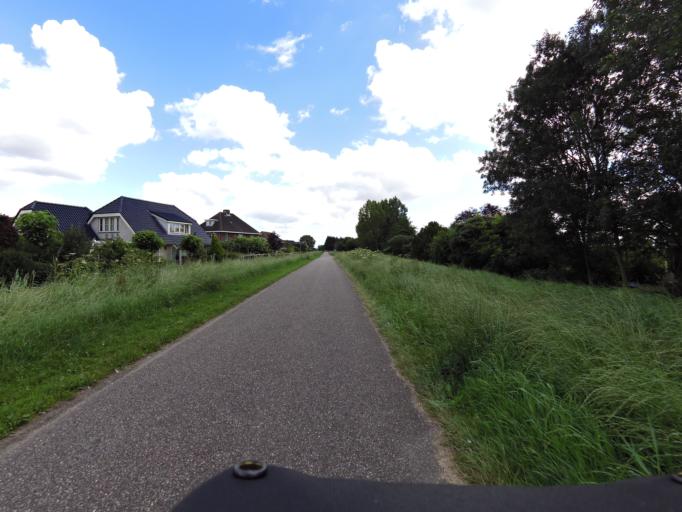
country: NL
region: South Holland
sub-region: Gemeente Spijkenisse
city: Spijkenisse
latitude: 51.8291
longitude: 4.3642
